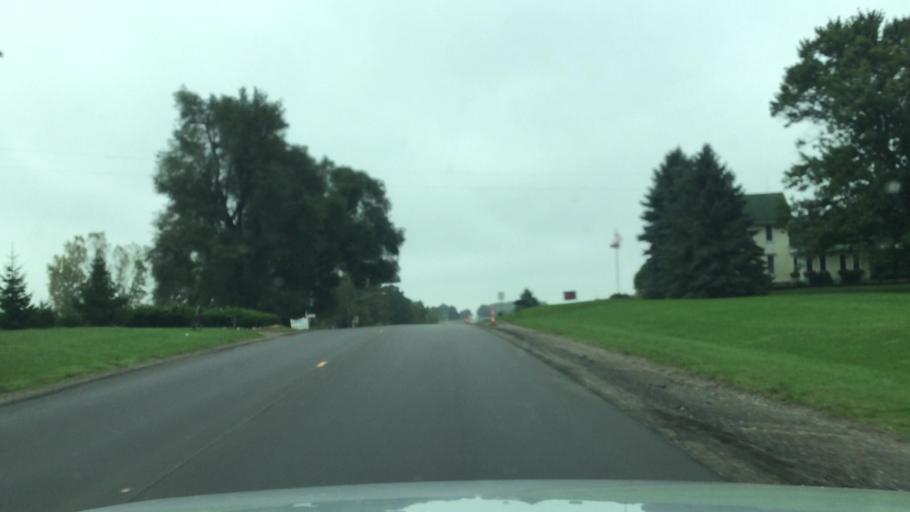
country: US
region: Michigan
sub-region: Shiawassee County
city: Perry
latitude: 42.8651
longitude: -84.2212
